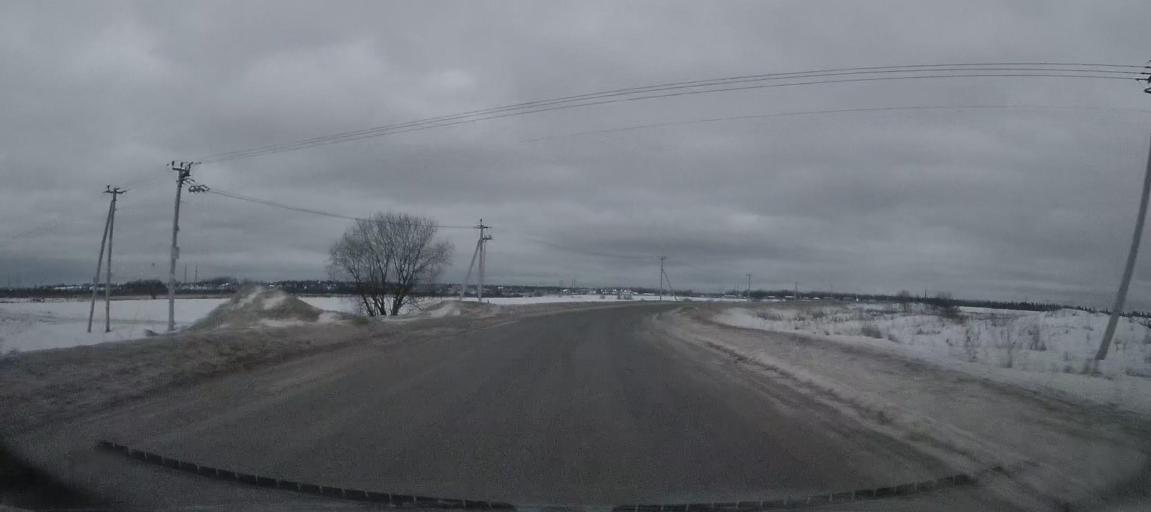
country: RU
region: Leningrad
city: Taytsy
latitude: 59.6889
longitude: 30.1360
